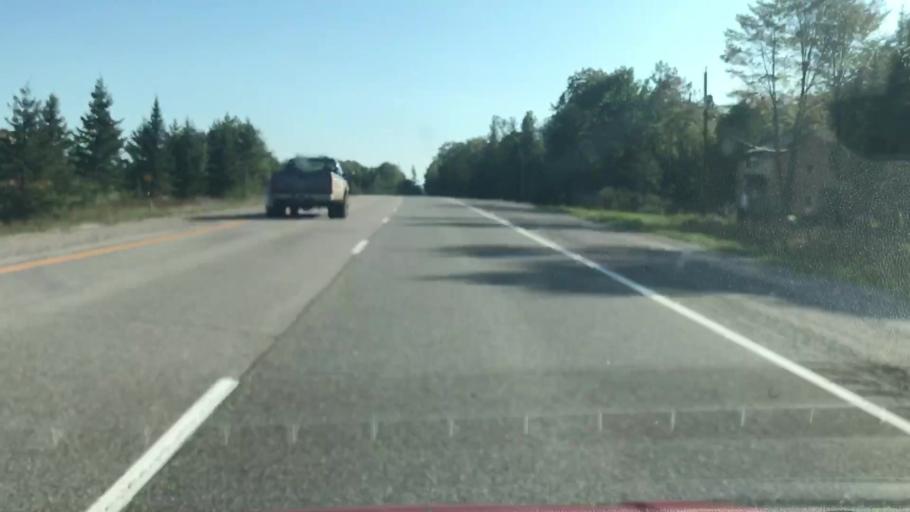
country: US
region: Michigan
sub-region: Chippewa County
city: Sault Ste. Marie
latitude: 46.3469
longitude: -84.0679
